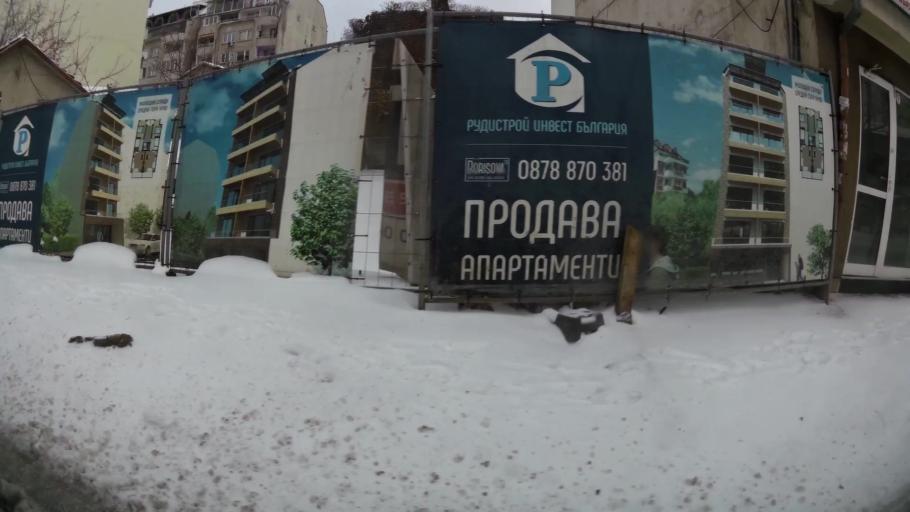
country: BG
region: Sofia-Capital
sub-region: Stolichna Obshtina
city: Sofia
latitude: 42.7033
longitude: 23.3121
